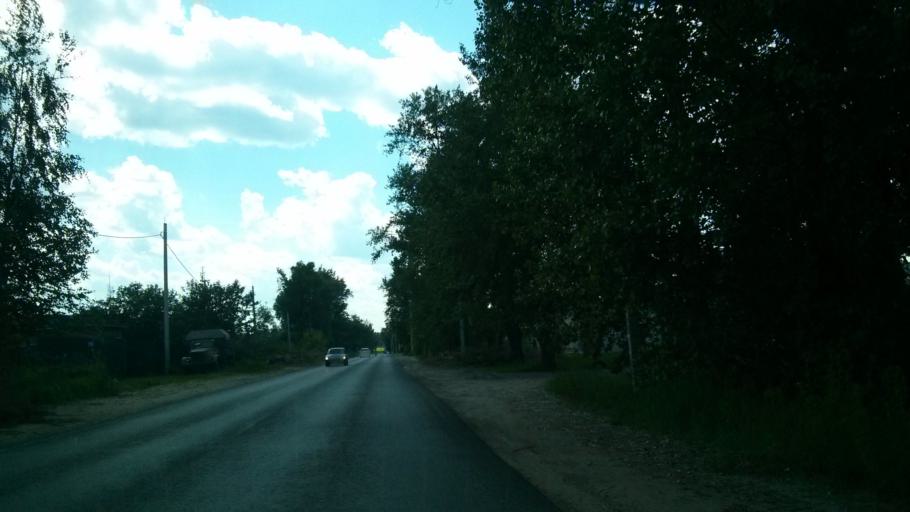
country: RU
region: Vladimir
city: Murom
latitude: 55.5325
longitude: 41.9665
